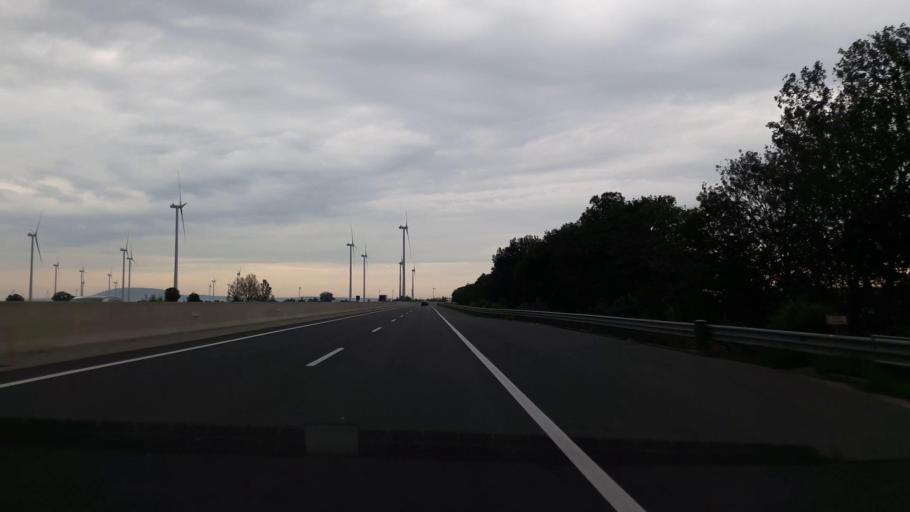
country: AT
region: Burgenland
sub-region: Politischer Bezirk Neusiedl am See
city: Parndorf
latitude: 48.0231
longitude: 16.8445
